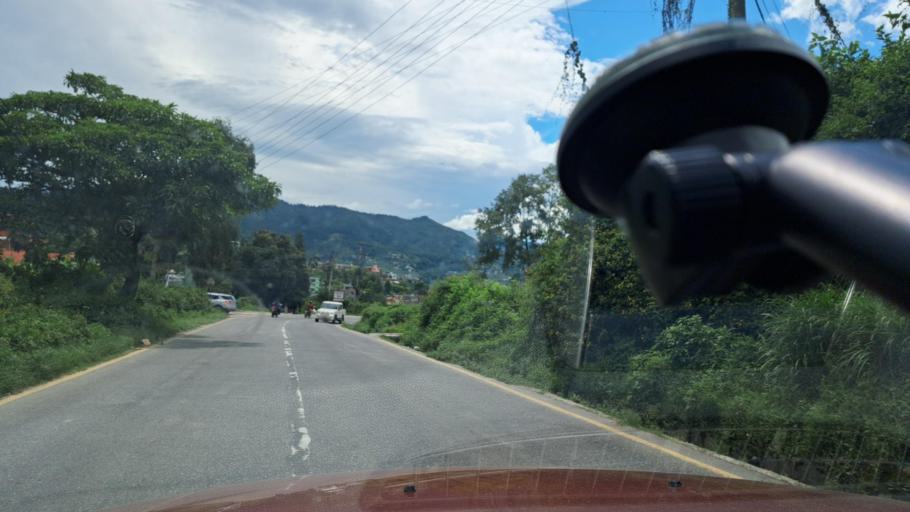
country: NP
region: Central Region
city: Banepa
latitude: 27.6255
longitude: 85.5452
